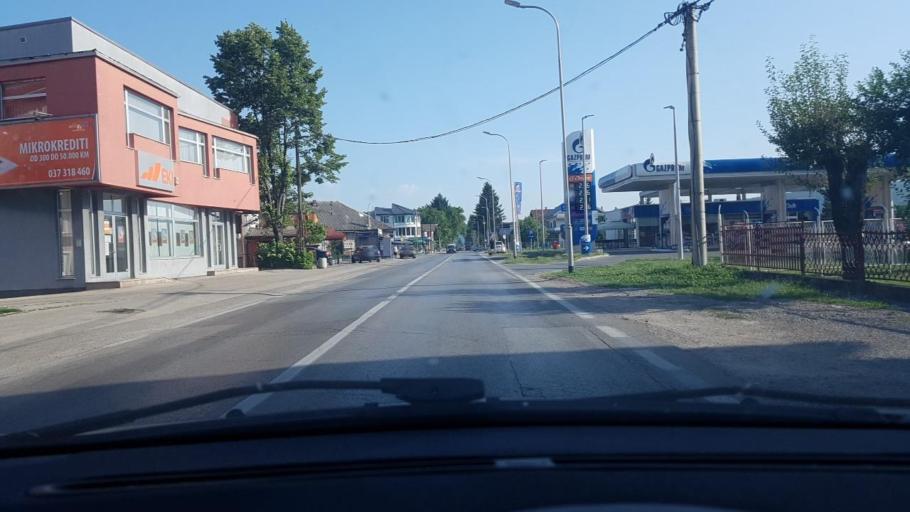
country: BA
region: Federation of Bosnia and Herzegovina
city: Bihac
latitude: 44.8195
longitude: 15.8817
